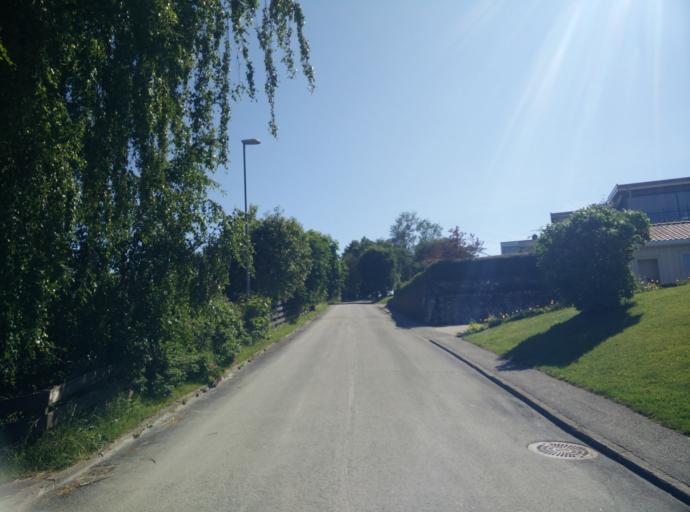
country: NO
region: Sor-Trondelag
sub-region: Trondheim
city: Trondheim
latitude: 63.4097
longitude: 10.3735
